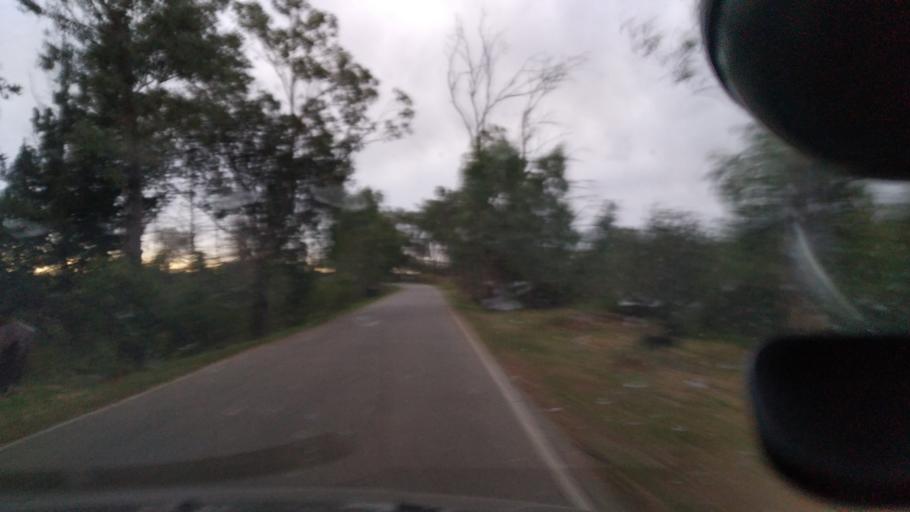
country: AR
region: Cordoba
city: Villa Las Rosas
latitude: -31.8792
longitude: -65.0255
